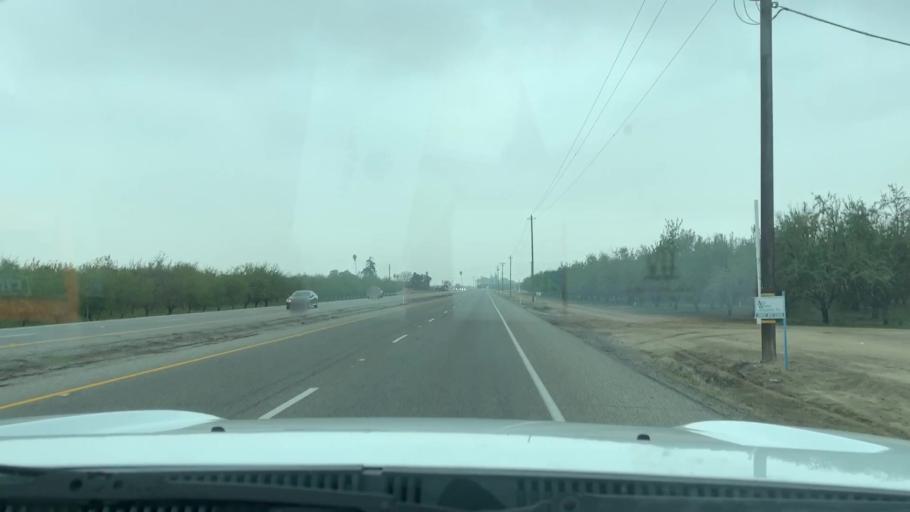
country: US
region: California
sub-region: Kern County
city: Wasco
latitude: 35.5534
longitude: -119.3321
